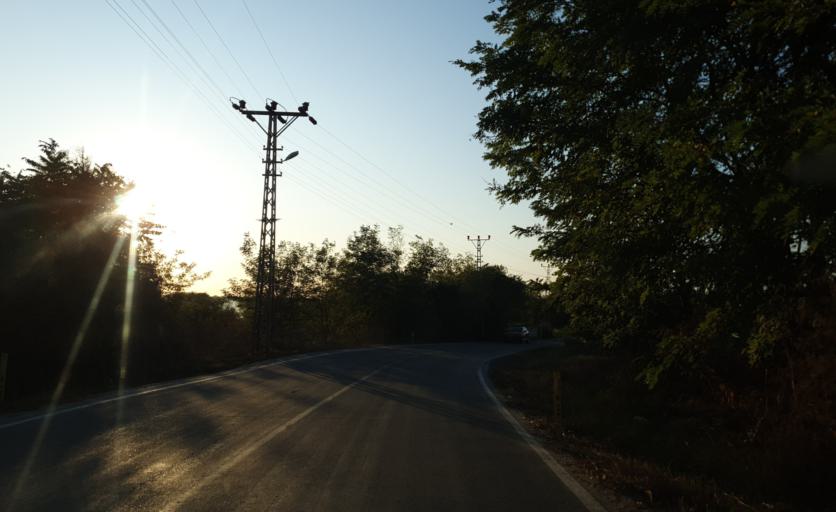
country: TR
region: Tekirdag
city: Beyazkoy
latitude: 41.3368
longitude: 27.7315
